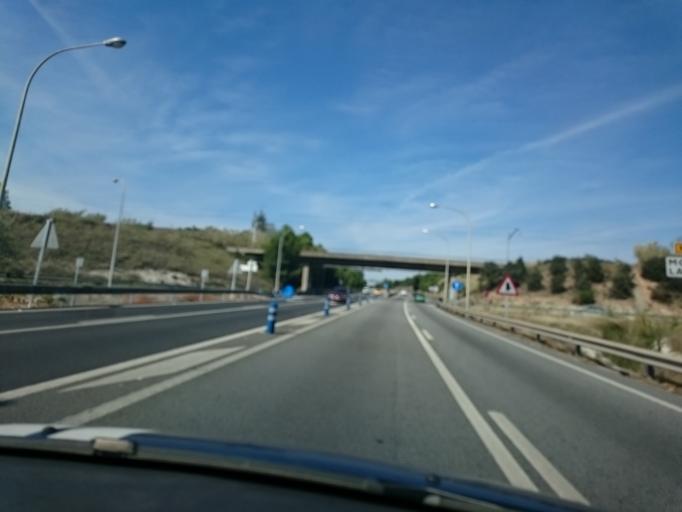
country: ES
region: Catalonia
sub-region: Provincia de Barcelona
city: Mollet del Valles
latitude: 41.5285
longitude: 2.2053
